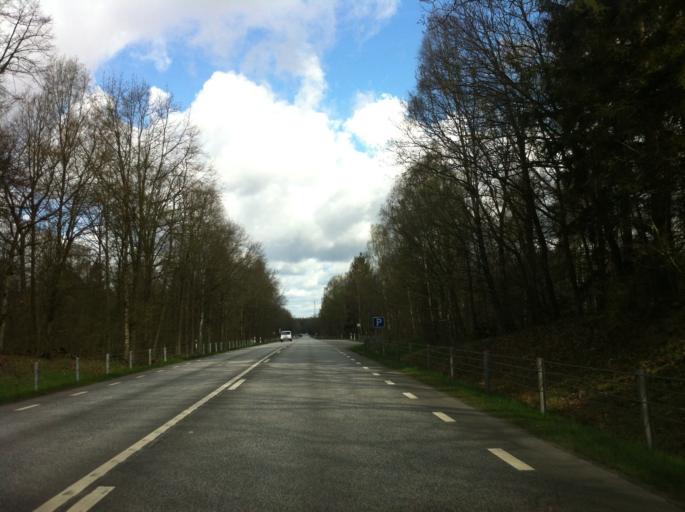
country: SE
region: Skane
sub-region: Horby Kommun
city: Hoerby
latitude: 55.8892
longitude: 13.6272
